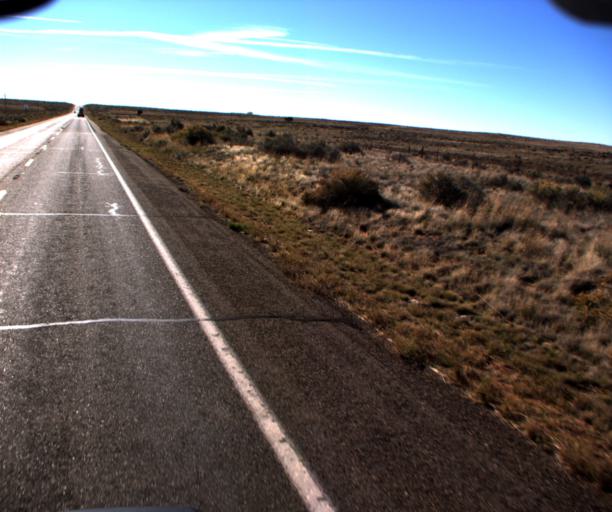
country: US
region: Arizona
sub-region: Mohave County
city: Colorado City
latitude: 36.9223
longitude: -112.9368
